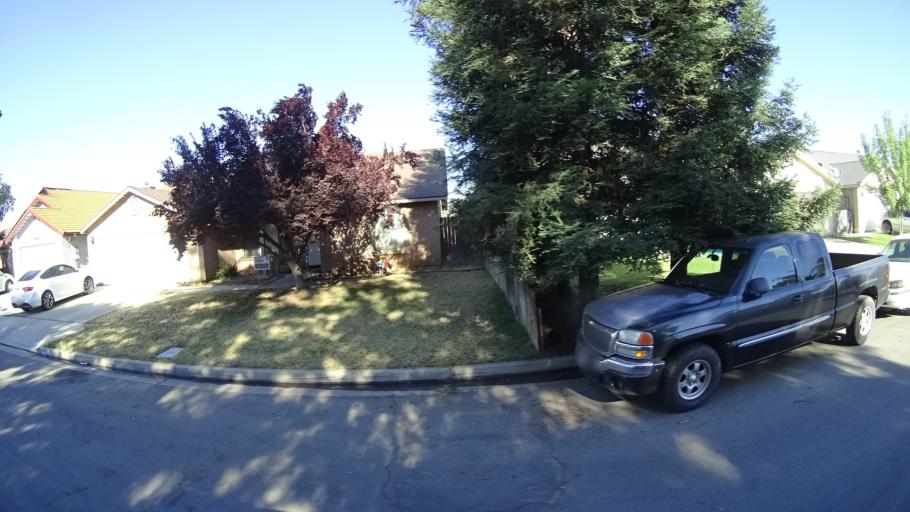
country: US
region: California
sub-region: Fresno County
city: West Park
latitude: 36.7847
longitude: -119.8664
